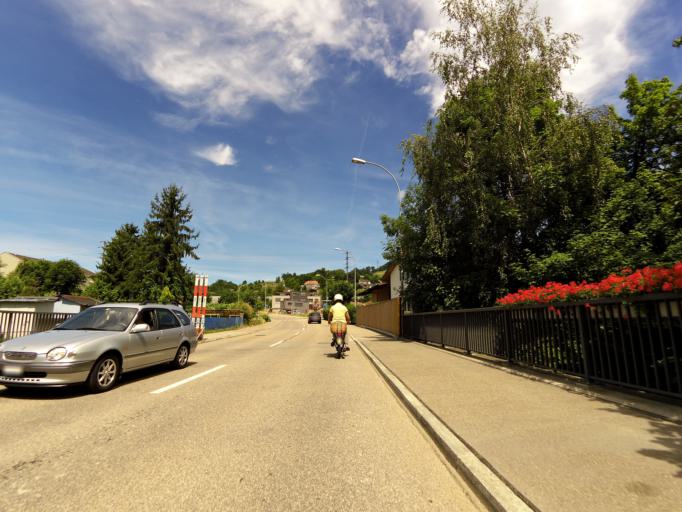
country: CH
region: Aargau
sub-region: Bezirk Laufenburg
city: Frick
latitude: 47.5083
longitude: 8.0217
